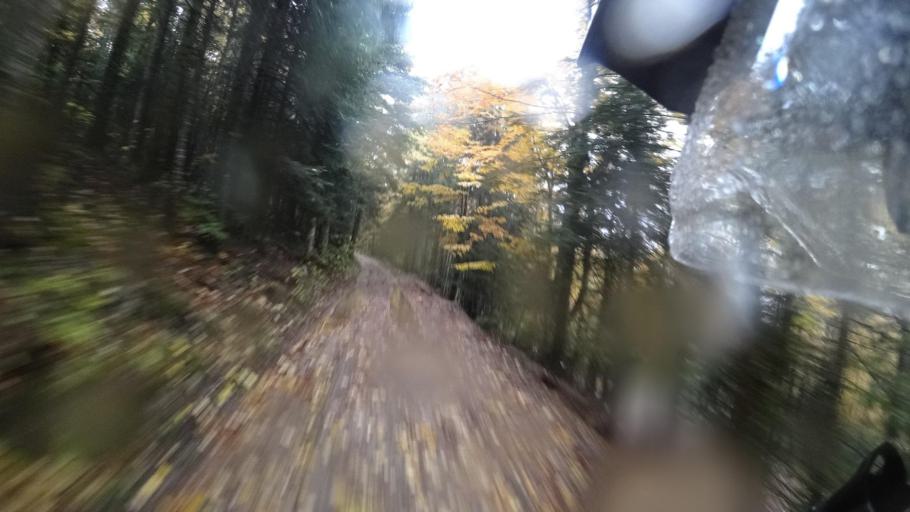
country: HR
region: Primorsko-Goranska
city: Vrbovsko
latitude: 45.3016
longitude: 15.0127
